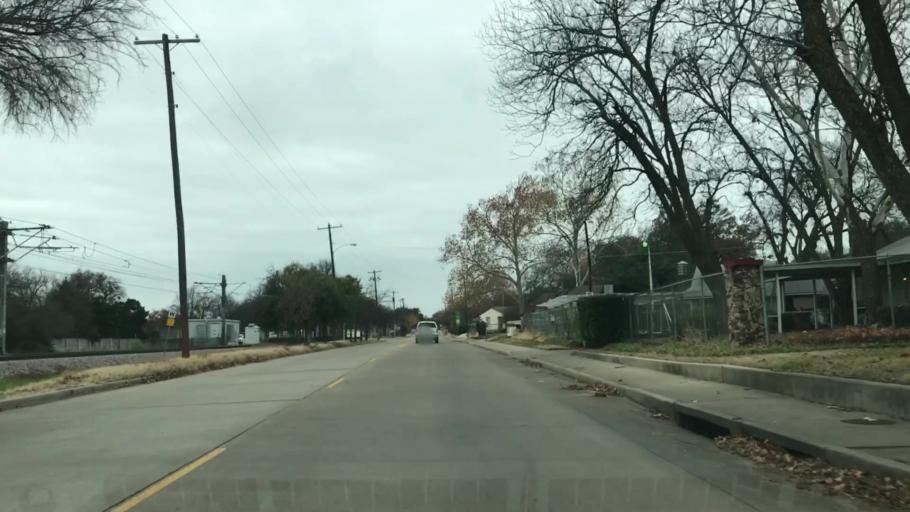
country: US
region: Texas
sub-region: Dallas County
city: Cockrell Hill
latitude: 32.7280
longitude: -96.8531
